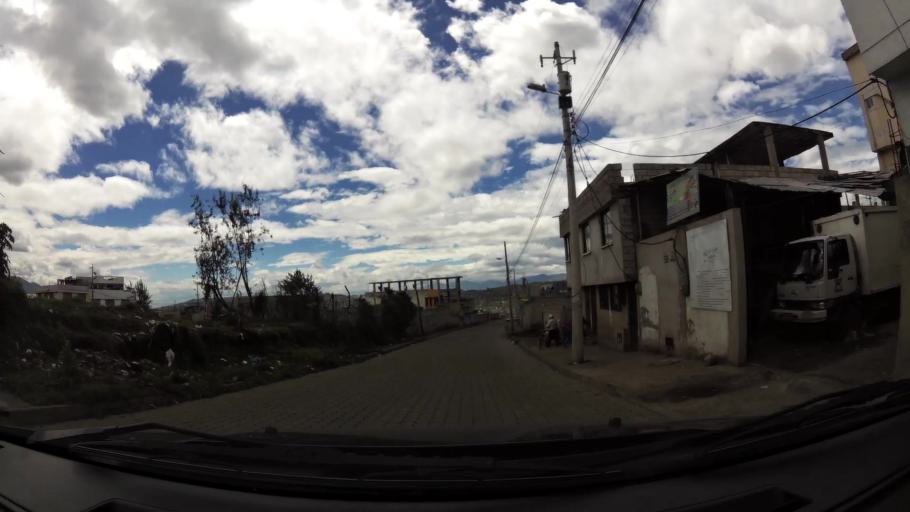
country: EC
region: Pichincha
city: Sangolqui
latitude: -0.3392
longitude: -78.5566
